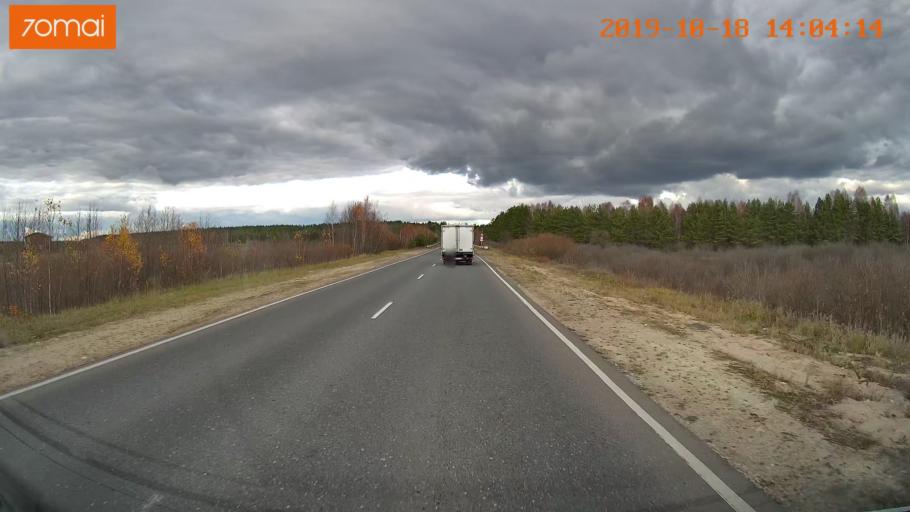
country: RU
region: Rjazan
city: Spas-Klepiki
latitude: 55.1237
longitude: 40.1335
